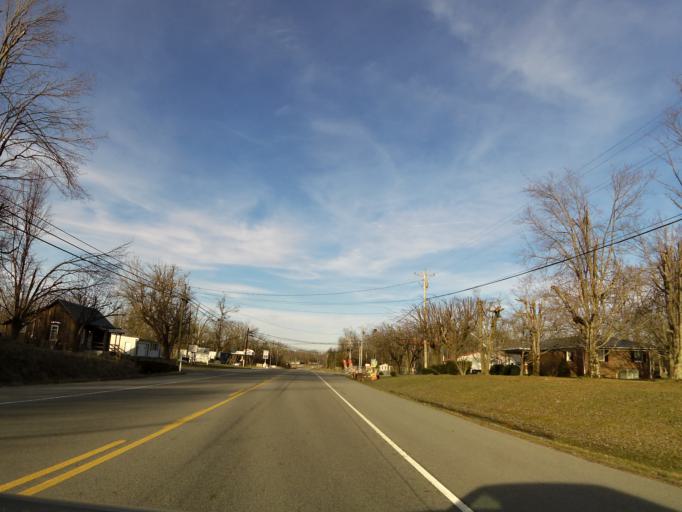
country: US
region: Tennessee
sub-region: White County
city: Sparta
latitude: 35.9496
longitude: -85.3098
